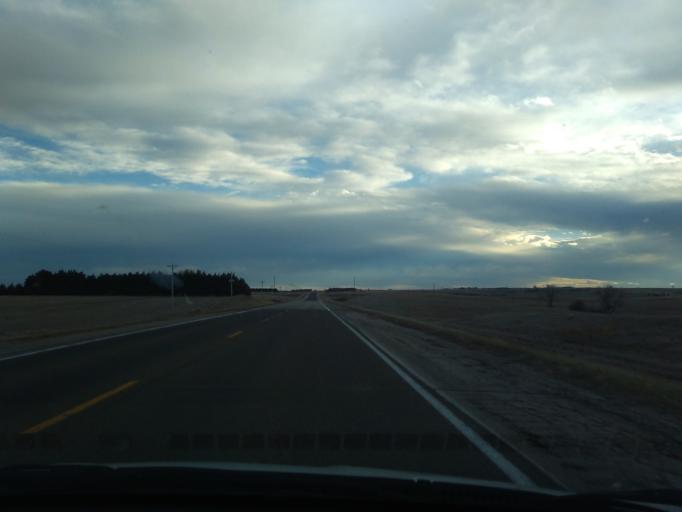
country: US
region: Nebraska
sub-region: Phelps County
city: Holdrege
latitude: 40.3420
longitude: -99.3687
